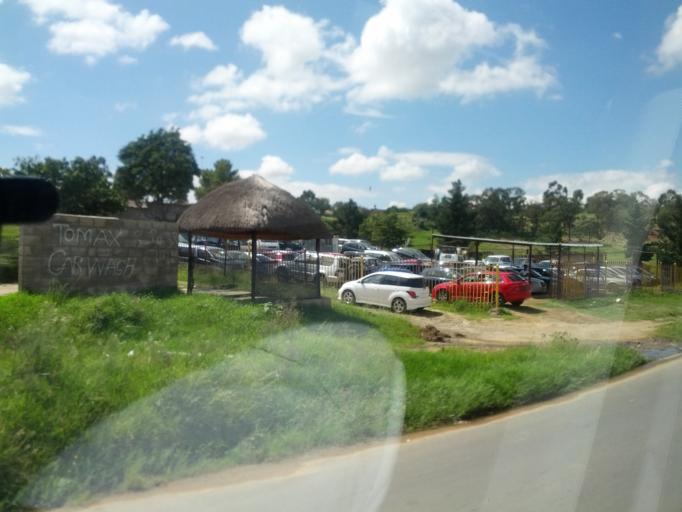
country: LS
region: Maseru
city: Maseru
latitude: -29.2962
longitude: 27.5176
